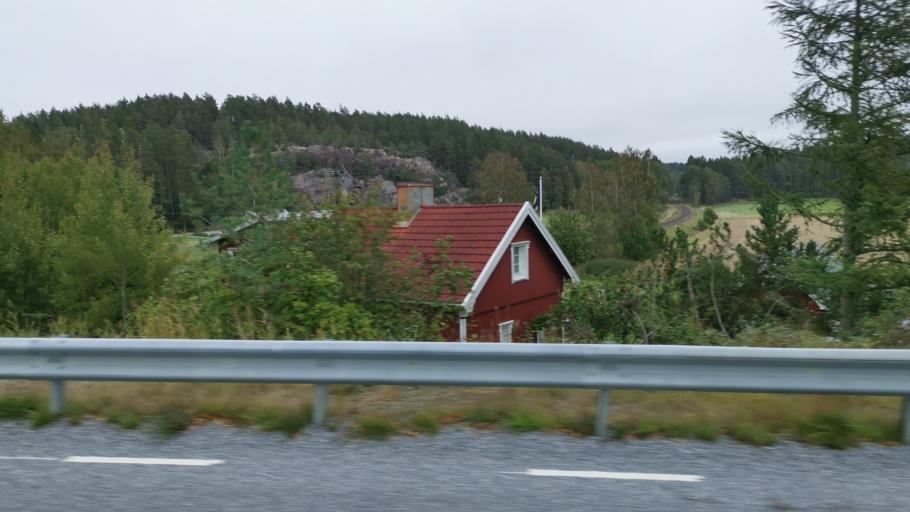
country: SE
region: Vaestra Goetaland
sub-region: Tanums Kommun
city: Tanumshede
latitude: 58.6709
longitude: 11.3408
